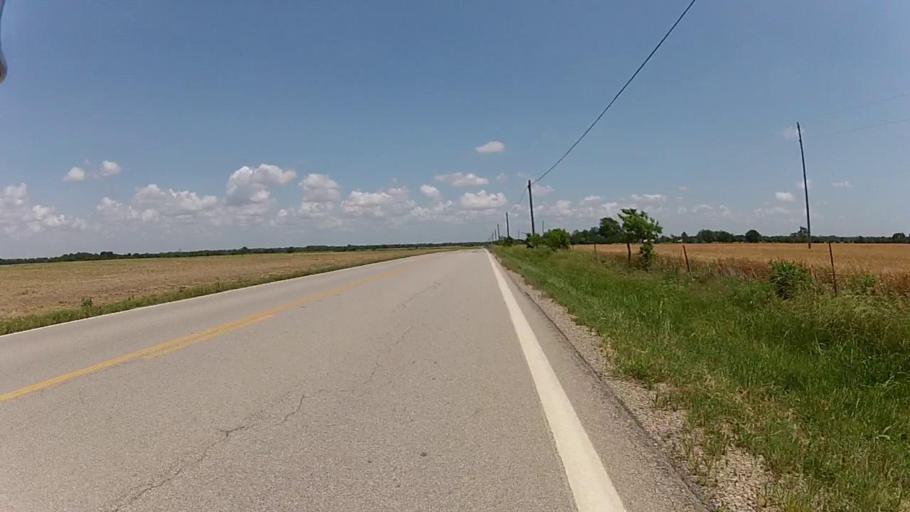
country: US
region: Kansas
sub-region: Labette County
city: Altamont
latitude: 37.1925
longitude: -95.4309
